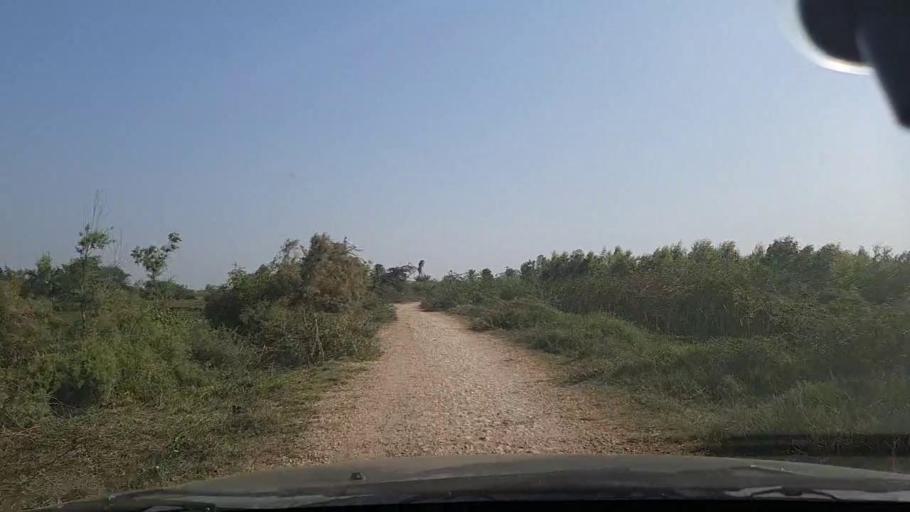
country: PK
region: Sindh
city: Chuhar Jamali
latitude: 24.5176
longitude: 67.8846
